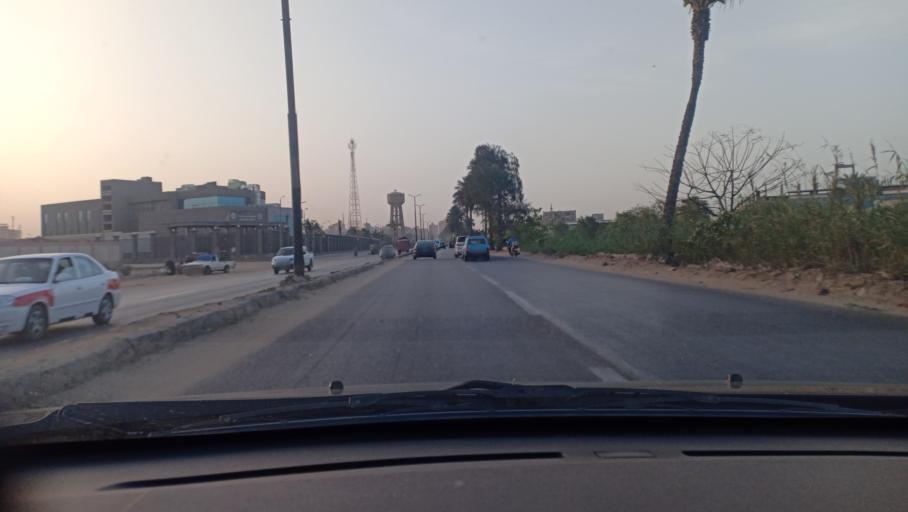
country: EG
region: Muhafazat al Gharbiyah
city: Zifta
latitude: 30.6978
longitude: 31.2750
